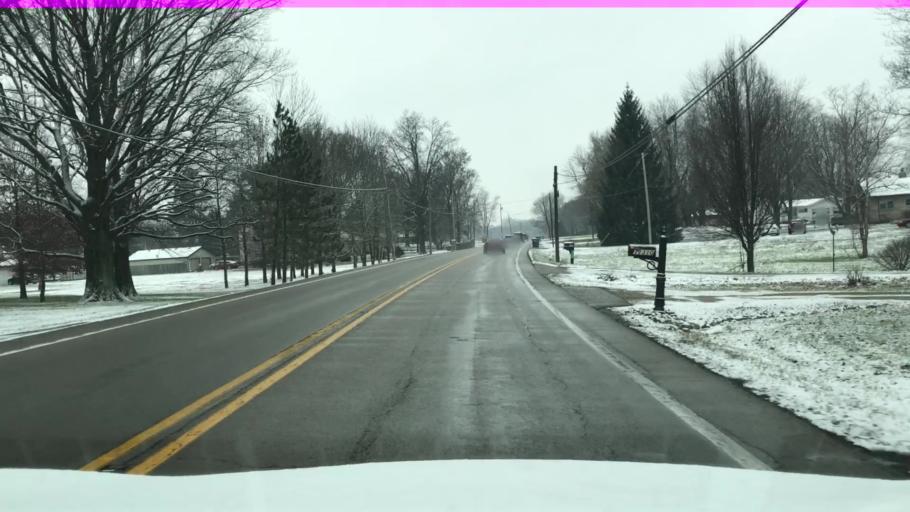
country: US
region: Indiana
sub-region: Delaware County
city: Yorktown
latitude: 40.1652
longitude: -85.5192
